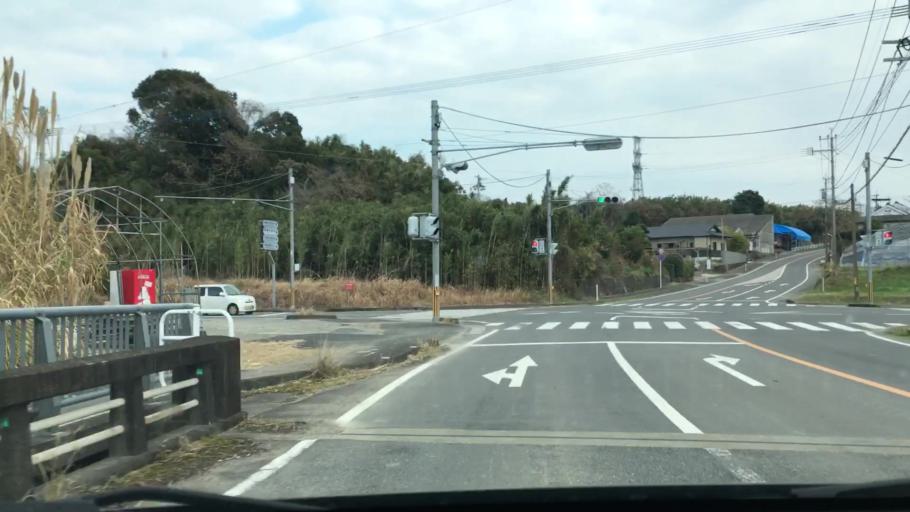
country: JP
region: Miyazaki
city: Kushima
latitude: 31.4678
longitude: 131.2146
